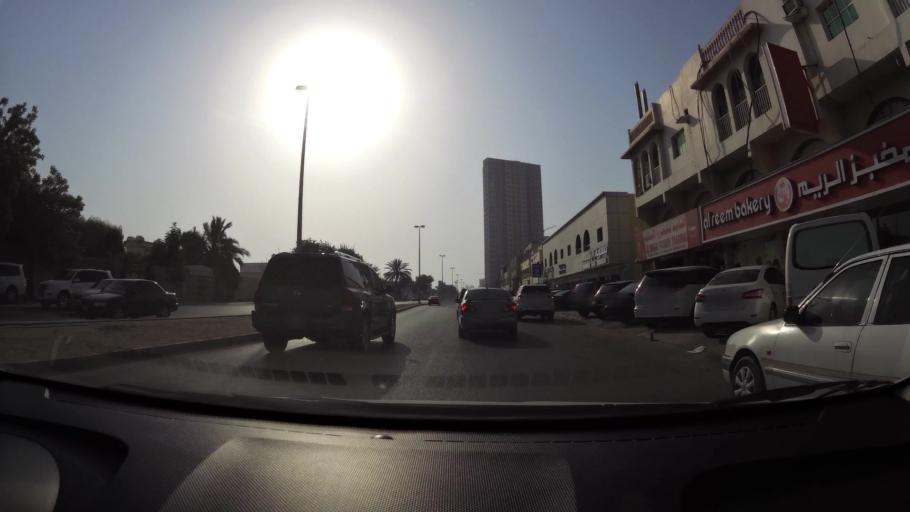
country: AE
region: Ajman
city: Ajman
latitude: 25.3857
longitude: 55.4410
